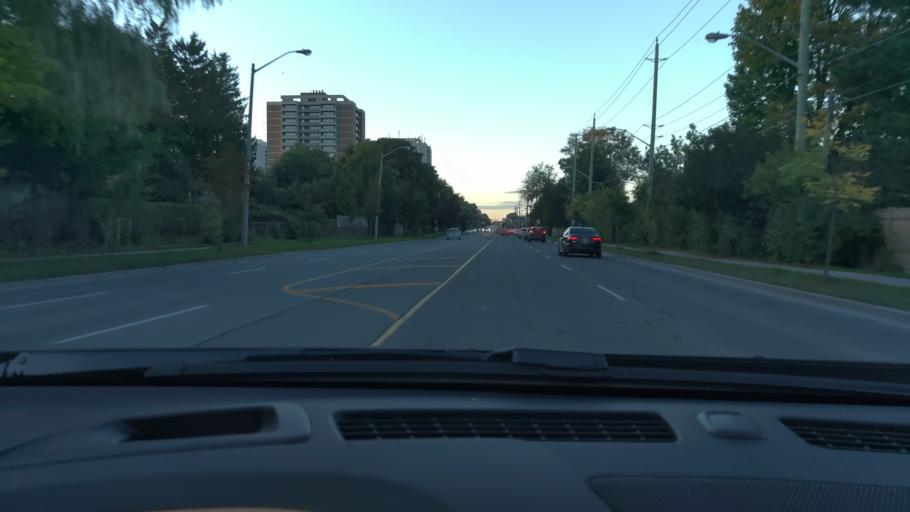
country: CA
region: Ontario
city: Willowdale
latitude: 43.7499
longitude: -79.3592
